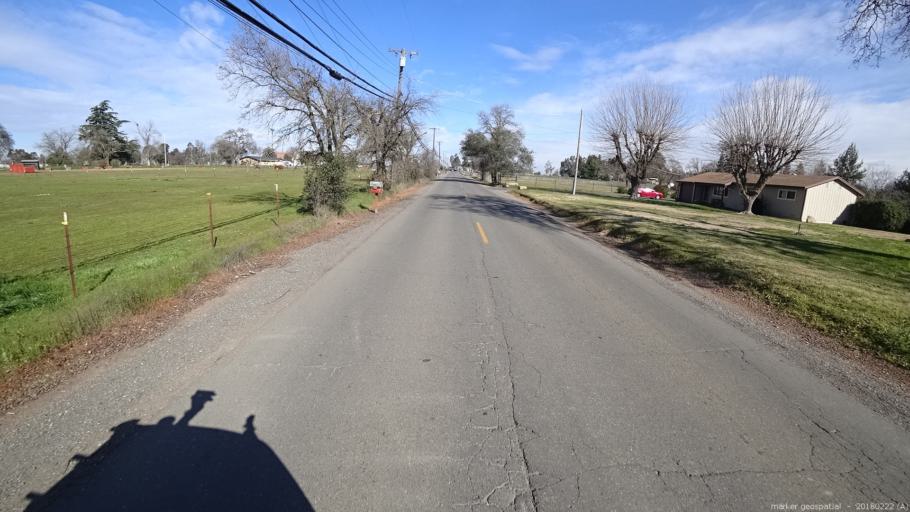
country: US
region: California
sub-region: Sacramento County
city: Rio Linda
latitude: 38.7005
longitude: -121.4291
